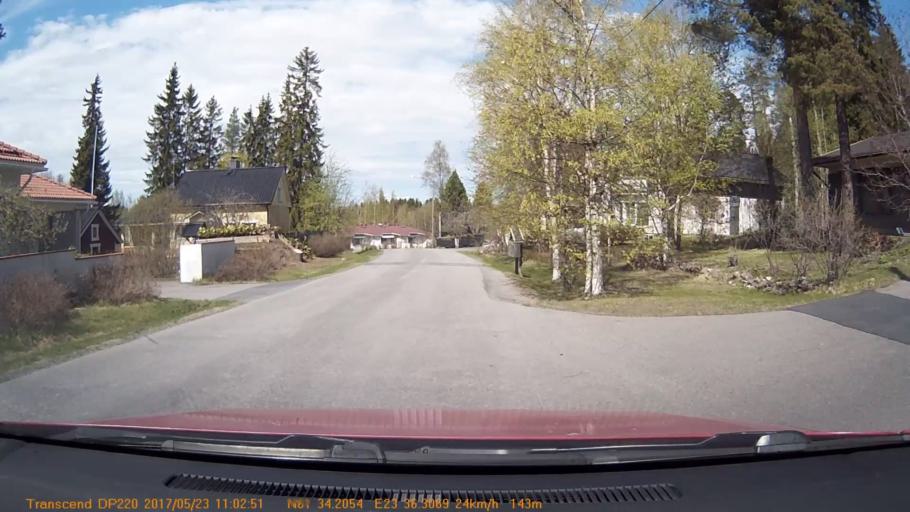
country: FI
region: Pirkanmaa
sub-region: Tampere
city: Yloejaervi
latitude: 61.5700
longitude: 23.6050
